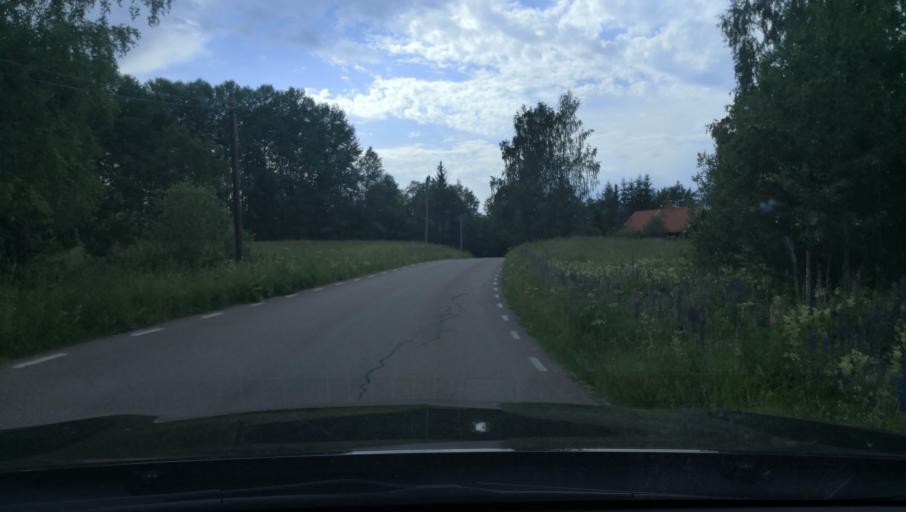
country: SE
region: Dalarna
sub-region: Smedjebackens Kommun
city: Smedjebacken
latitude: 60.0486
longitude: 15.5337
